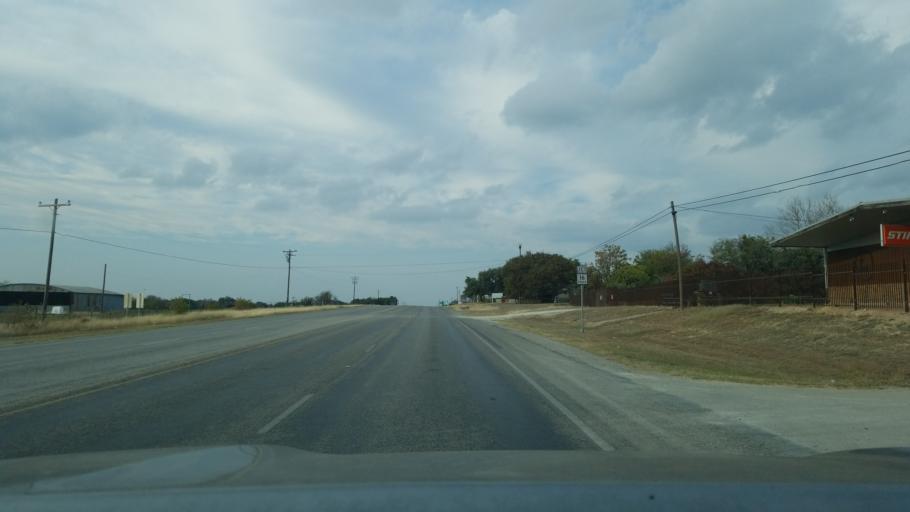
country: US
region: Texas
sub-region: Mills County
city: Goldthwaite
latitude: 31.4801
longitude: -98.5701
